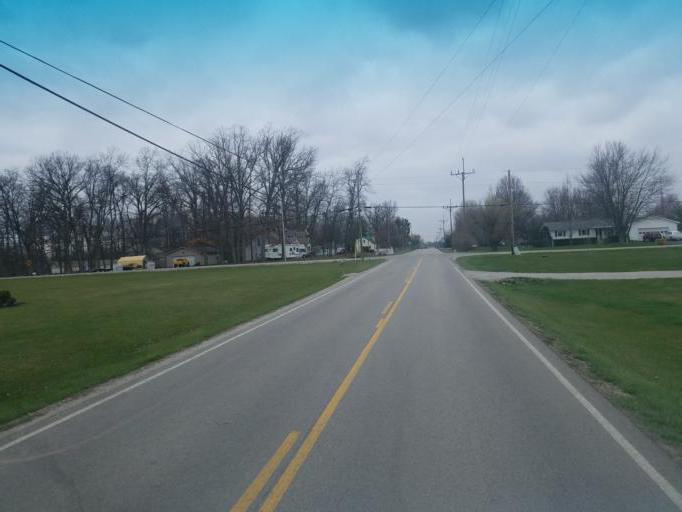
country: US
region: Ohio
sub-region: Marion County
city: Marion
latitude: 40.5341
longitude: -83.1507
